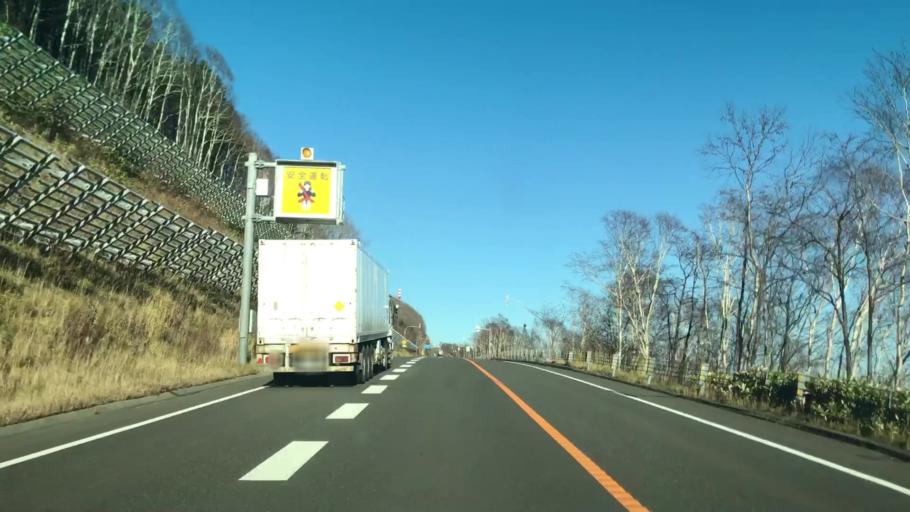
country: JP
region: Hokkaido
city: Otofuke
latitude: 42.9632
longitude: 142.7907
